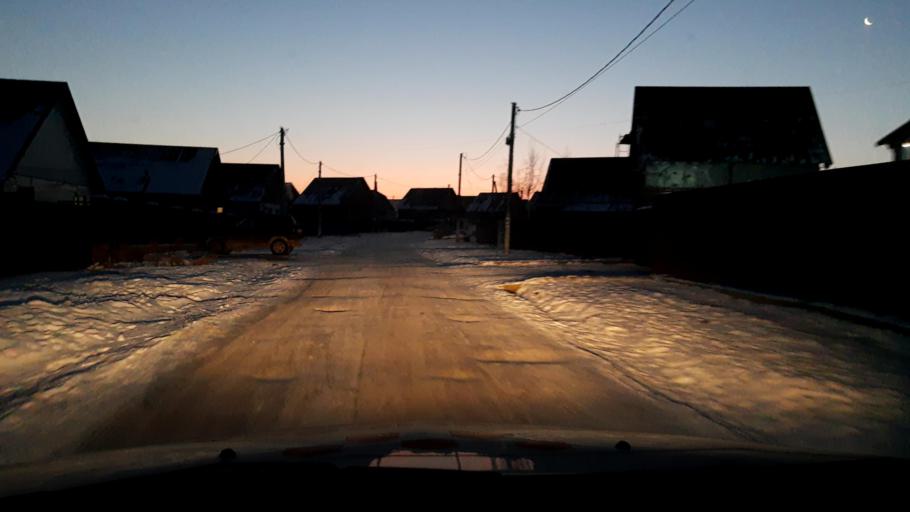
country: RU
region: Bashkortostan
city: Iglino
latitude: 54.8280
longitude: 56.4337
